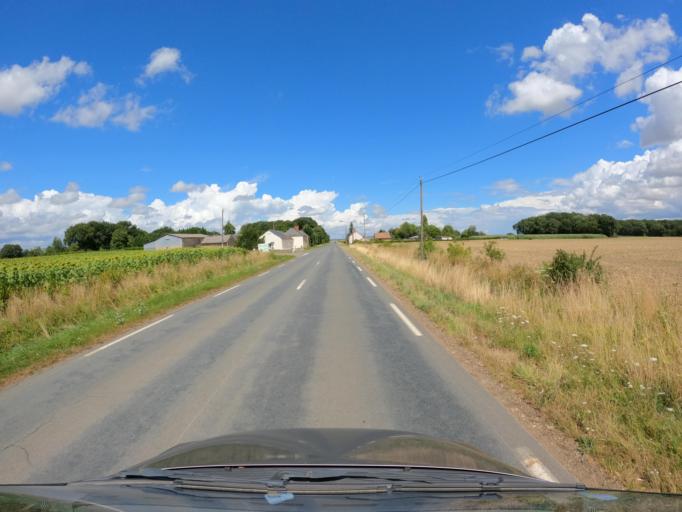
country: FR
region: Pays de la Loire
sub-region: Departement de la Sarthe
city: Juigne-sur-Sarthe
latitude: 47.9040
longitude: -0.2792
